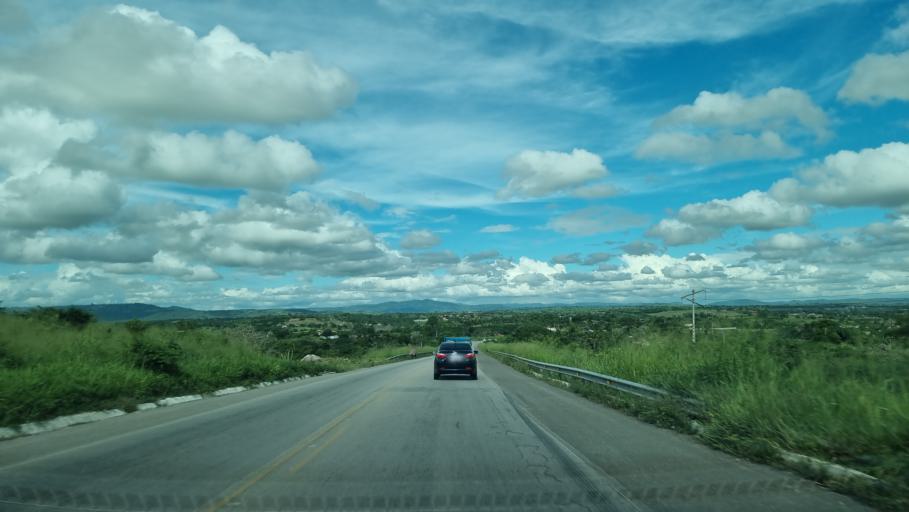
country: BR
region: Pernambuco
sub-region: Agrestina
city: Agrestina
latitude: -8.3869
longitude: -35.9785
